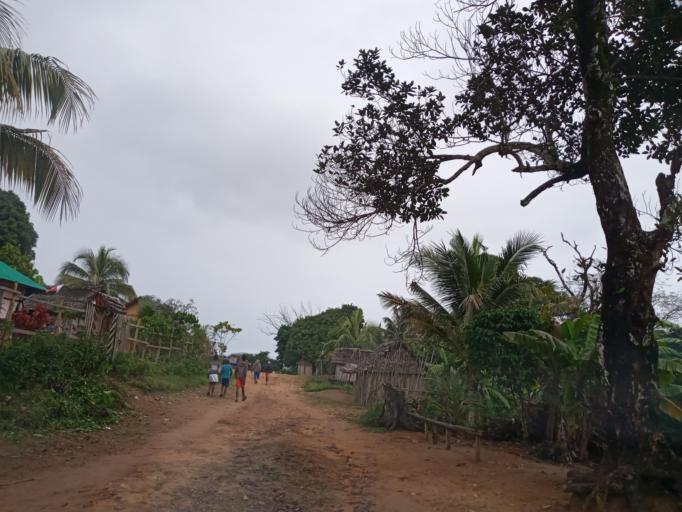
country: MG
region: Atsimo-Atsinanana
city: Vohipaho
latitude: -23.9731
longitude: 47.3339
